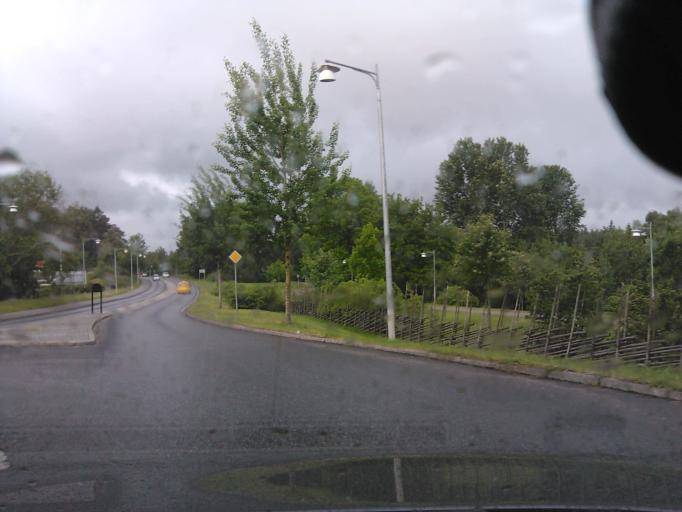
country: SE
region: Stockholm
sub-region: Vallentuna Kommun
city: Vallentuna
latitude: 59.4990
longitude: 18.0635
